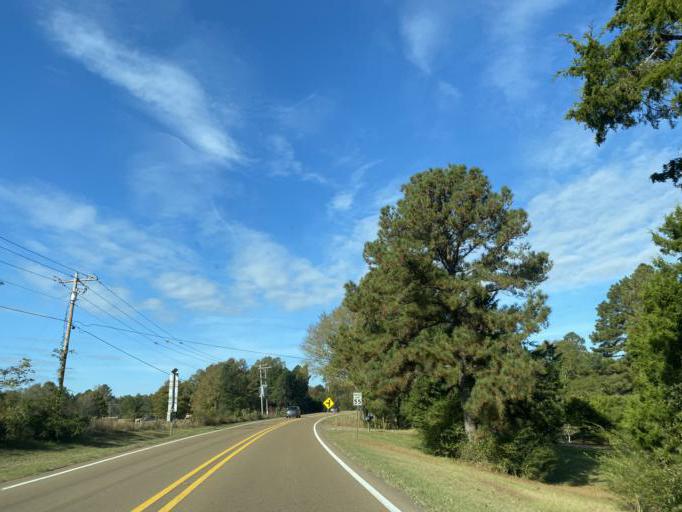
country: US
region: Mississippi
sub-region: Madison County
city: Madison
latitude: 32.4820
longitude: -90.1727
